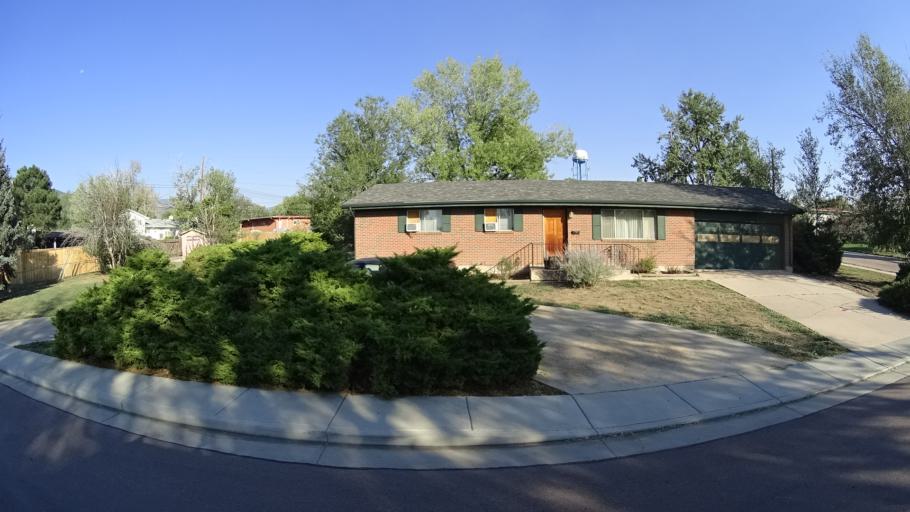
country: US
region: Colorado
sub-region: El Paso County
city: Stratmoor
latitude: 38.7758
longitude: -104.7961
